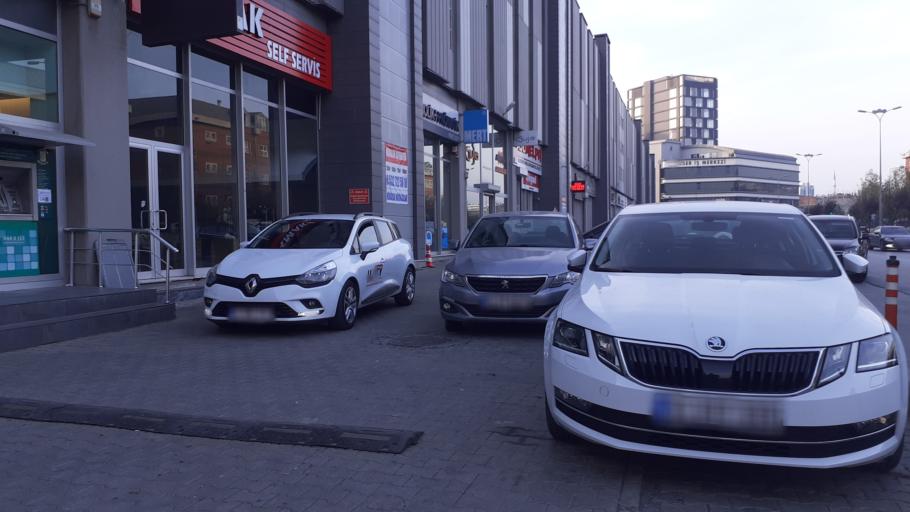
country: TR
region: Istanbul
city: Basaksehir
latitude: 41.0715
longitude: 28.7946
